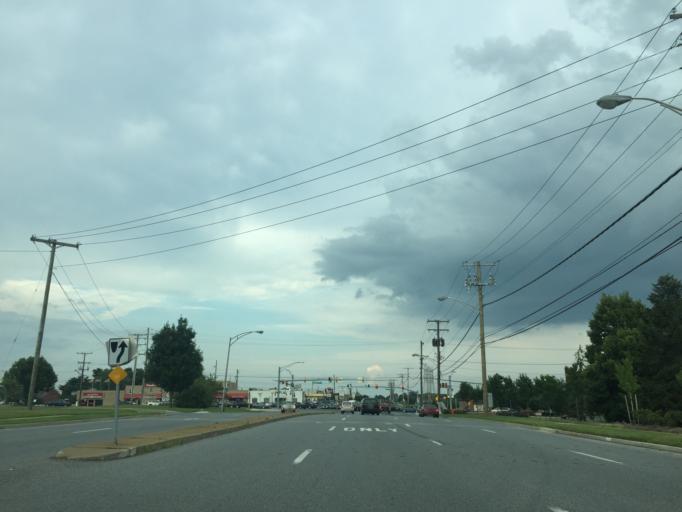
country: US
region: Maryland
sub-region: Baltimore County
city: Dundalk
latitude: 39.2705
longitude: -76.5048
